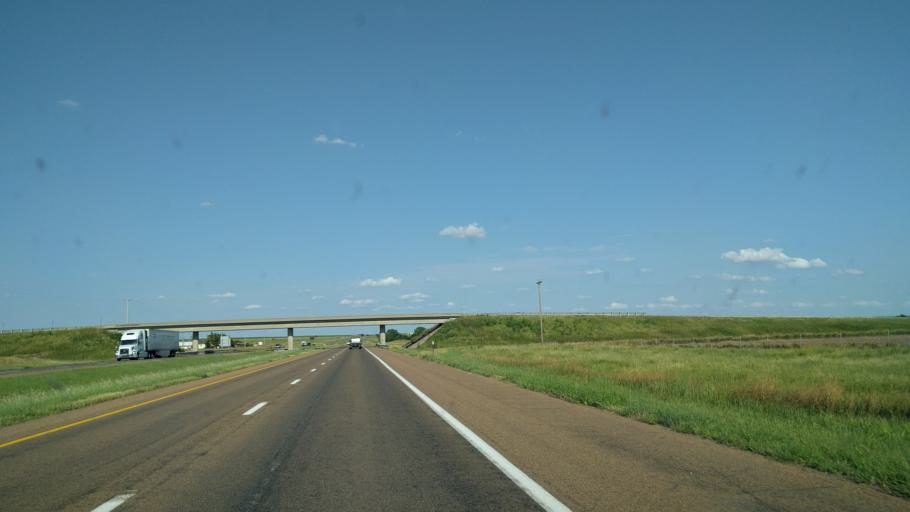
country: US
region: Kansas
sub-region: Ellis County
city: Ellis
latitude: 38.9495
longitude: -99.5413
